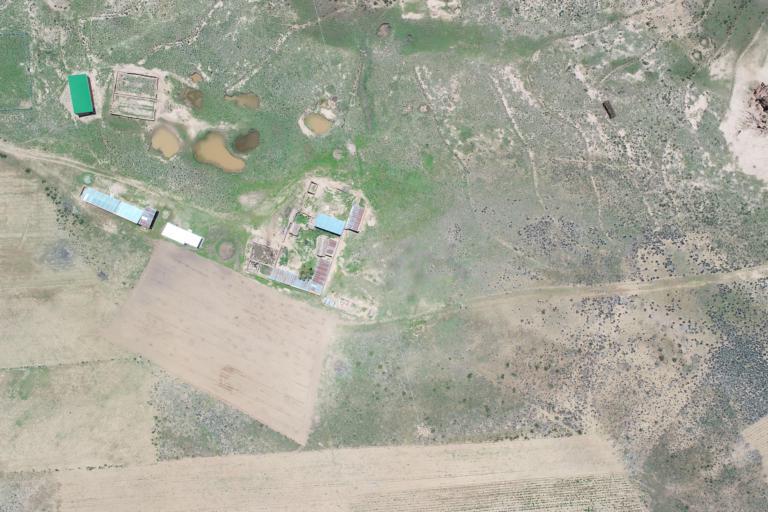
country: BO
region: La Paz
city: Curahuara de Carangas
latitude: -17.3097
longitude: -68.5078
